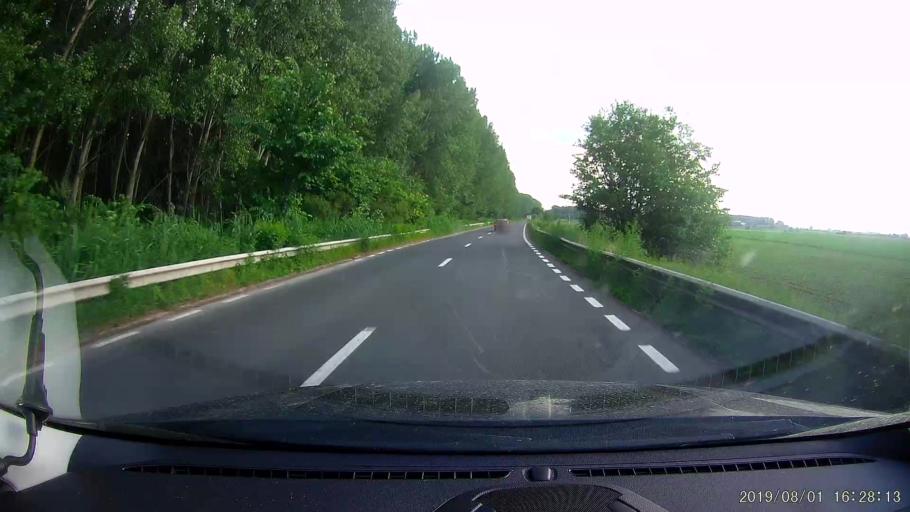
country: RO
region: Calarasi
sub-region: Municipiul Calarasi
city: Calarasi
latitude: 44.1509
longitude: 27.3119
